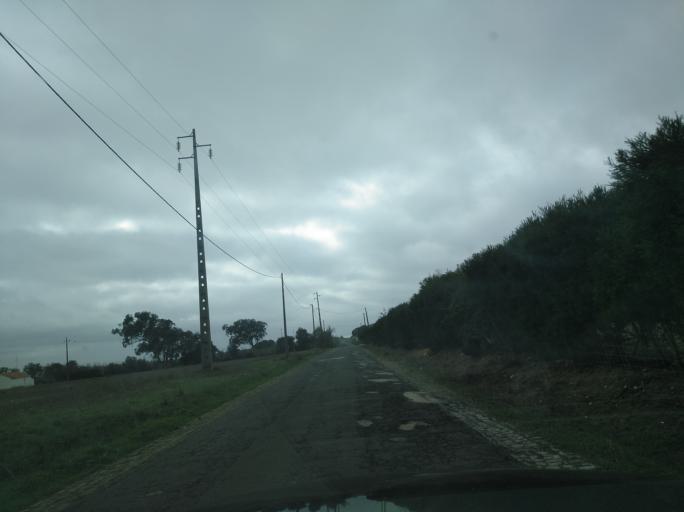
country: PT
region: Setubal
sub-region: Sines
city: Porto Covo
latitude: 37.8436
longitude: -8.7764
